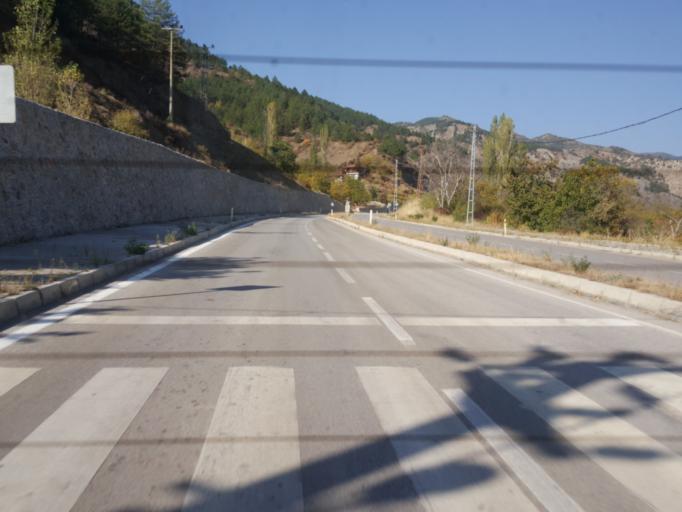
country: TR
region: Corum
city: Iskilip
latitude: 40.7373
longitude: 34.4542
